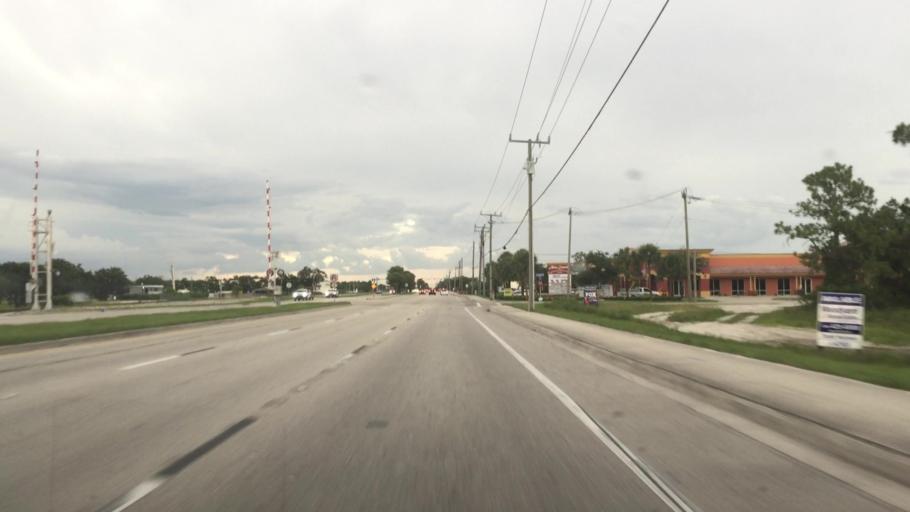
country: US
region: Florida
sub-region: Lee County
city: San Carlos Park
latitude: 26.4926
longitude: -81.8300
